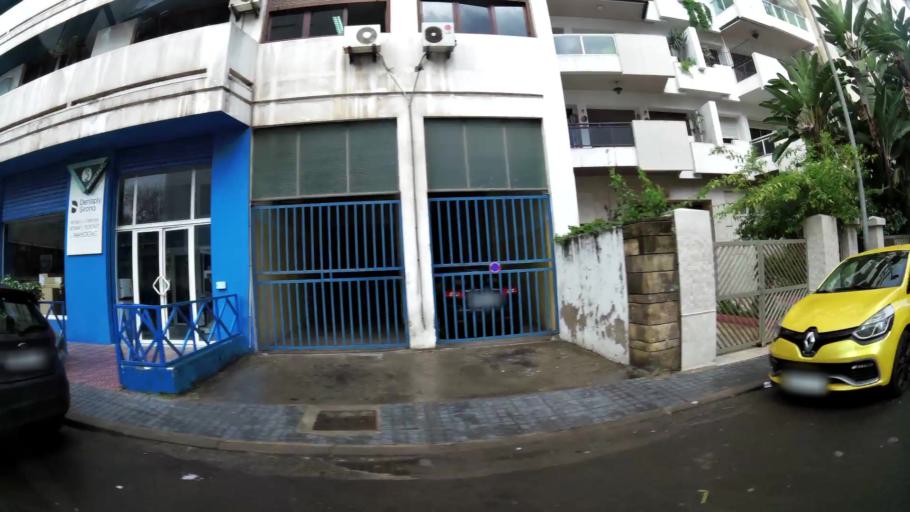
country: MA
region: Grand Casablanca
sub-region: Casablanca
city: Casablanca
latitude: 33.5833
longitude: -7.6166
